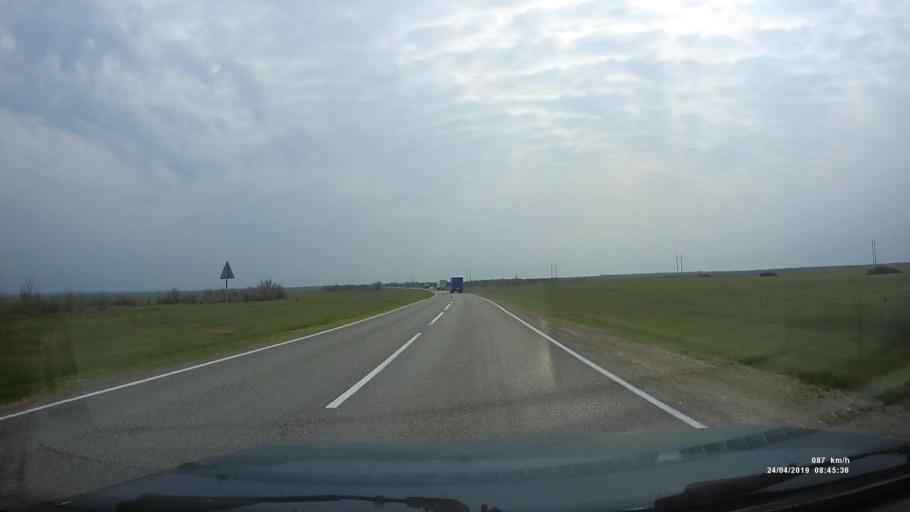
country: RU
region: Kalmykiya
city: Arshan'
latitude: 46.2359
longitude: 44.0638
